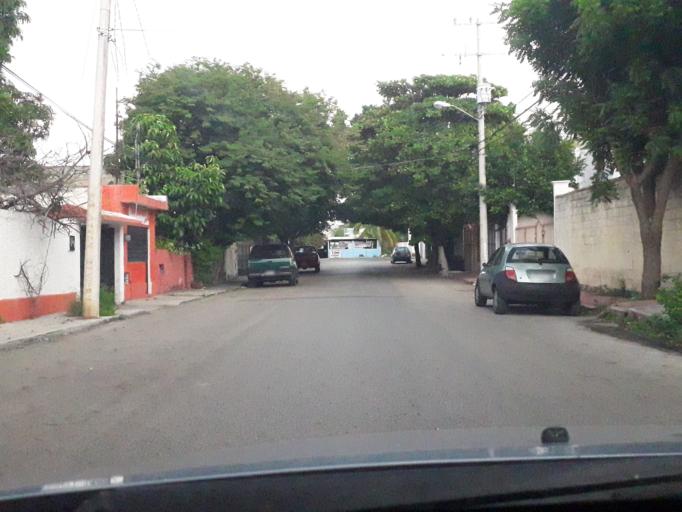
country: MX
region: Yucatan
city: Merida
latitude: 21.0191
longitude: -89.6325
